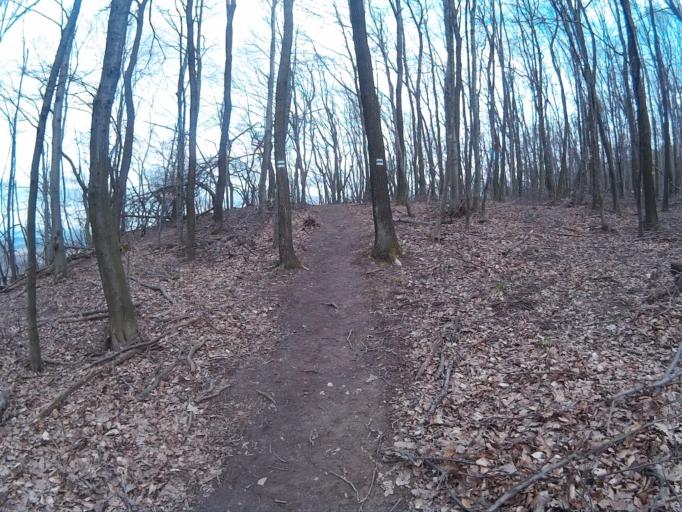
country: HU
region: Pest
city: Kosd
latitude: 47.8370
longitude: 19.1449
